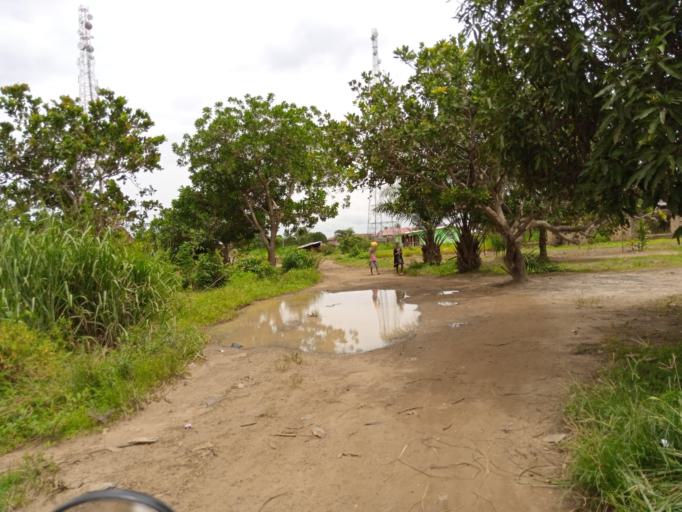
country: SL
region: Southern Province
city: Moyamba
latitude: 8.1677
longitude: -12.4188
